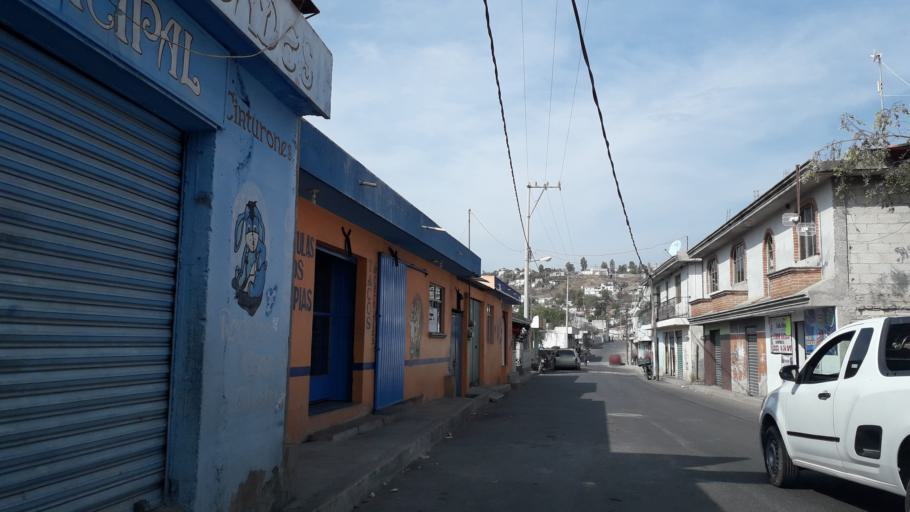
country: MX
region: Puebla
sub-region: Puebla
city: San Andres Azumiatla
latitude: 18.9026
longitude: -98.2536
